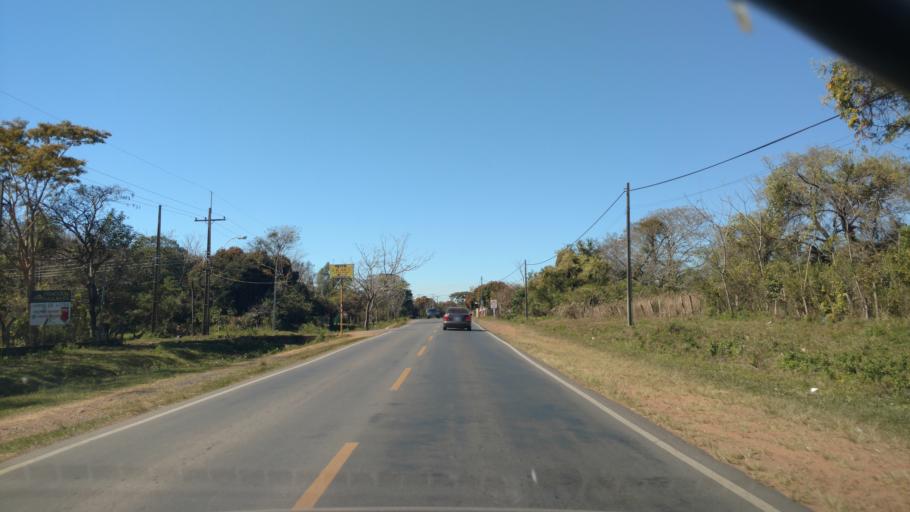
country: PY
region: Paraguari
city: Pirayu
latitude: -25.4785
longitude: -57.2441
